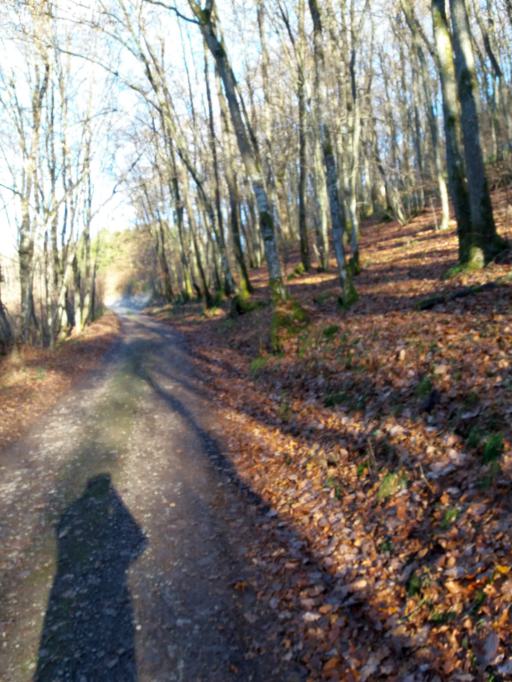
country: LU
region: Diekirch
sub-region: Canton de Diekirch
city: Bourscheid
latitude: 49.9178
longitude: 6.0410
